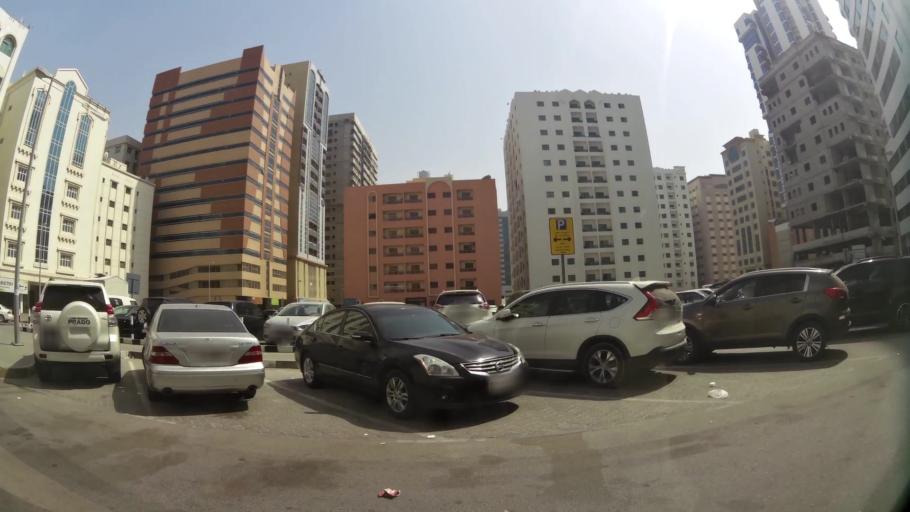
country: AE
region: Ash Shariqah
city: Sharjah
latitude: 25.3499
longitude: 55.3924
